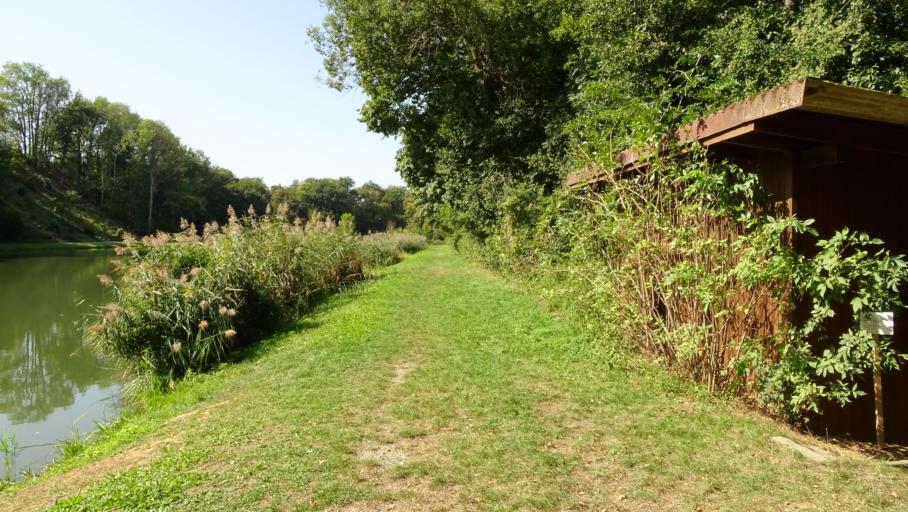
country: DE
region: Baden-Wuerttemberg
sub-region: Karlsruhe Region
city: Billigheim
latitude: 49.3508
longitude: 9.2748
